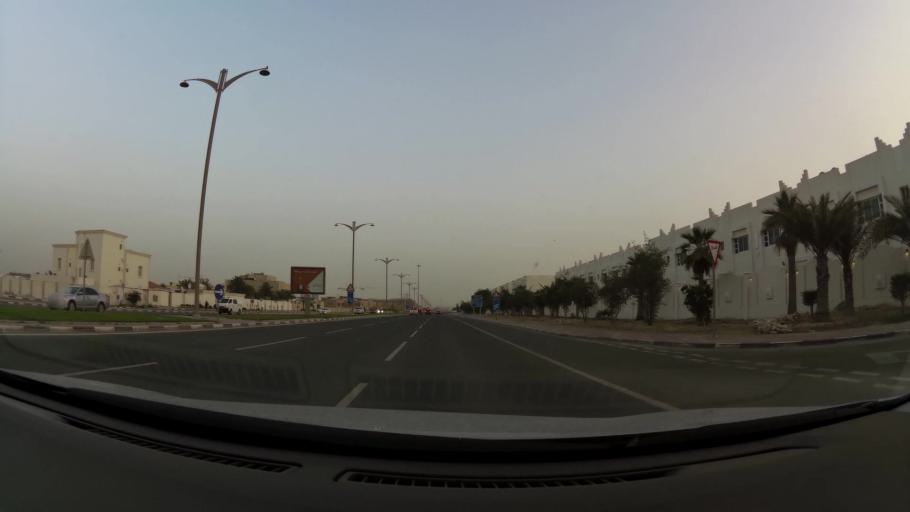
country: QA
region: Baladiyat ar Rayyan
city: Ar Rayyan
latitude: 25.2622
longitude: 51.4650
